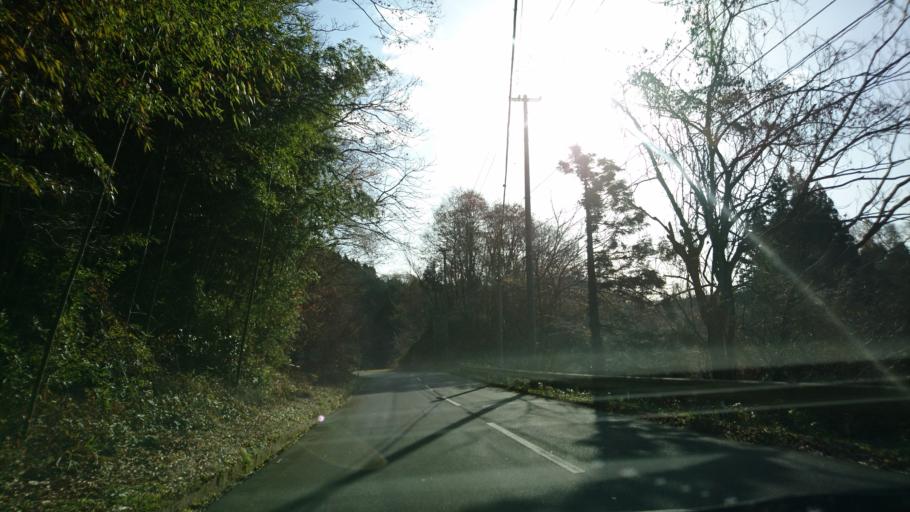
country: JP
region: Iwate
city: Ichinoseki
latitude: 38.8687
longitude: 141.3262
